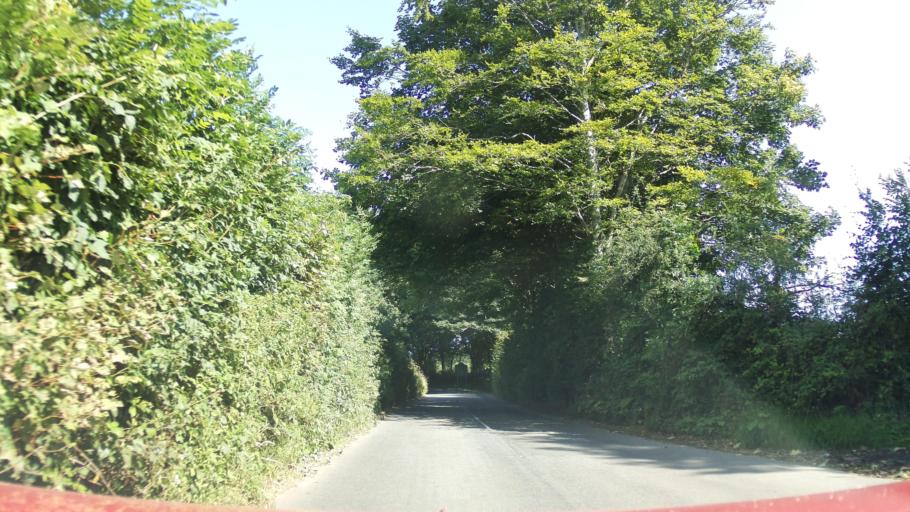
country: GB
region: England
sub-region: Devon
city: Tavistock
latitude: 50.5522
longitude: -4.1204
